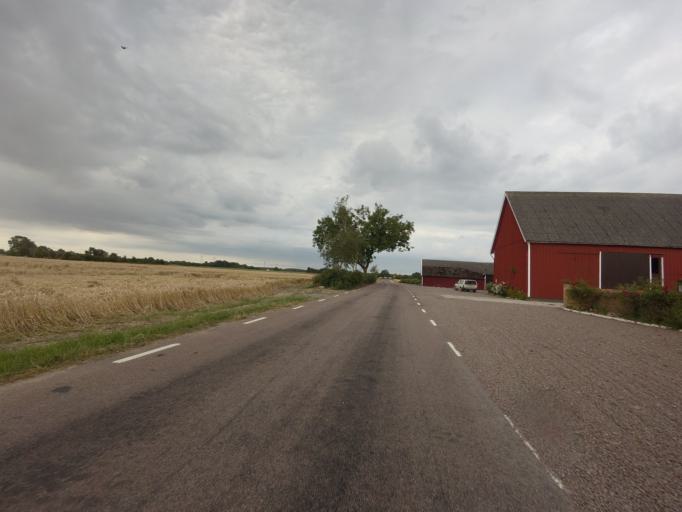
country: SE
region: Skane
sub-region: Helsingborg
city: Odakra
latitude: 56.1428
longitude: 12.7308
